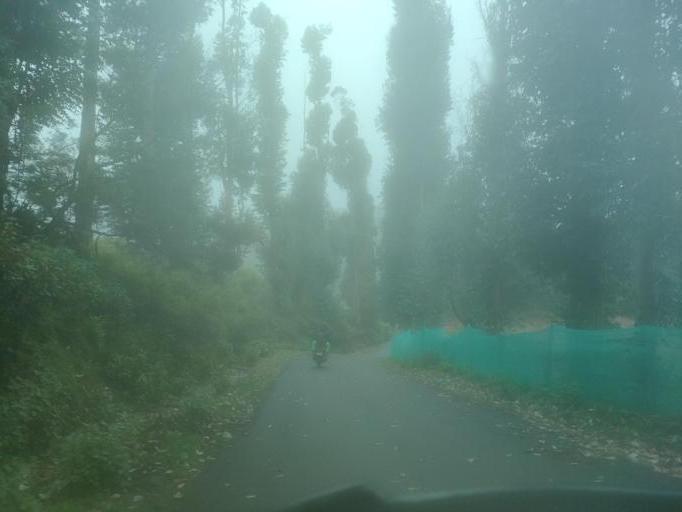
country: IN
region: Tamil Nadu
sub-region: Dindigul
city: Kodaikanal
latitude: 10.2064
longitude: 77.3474
